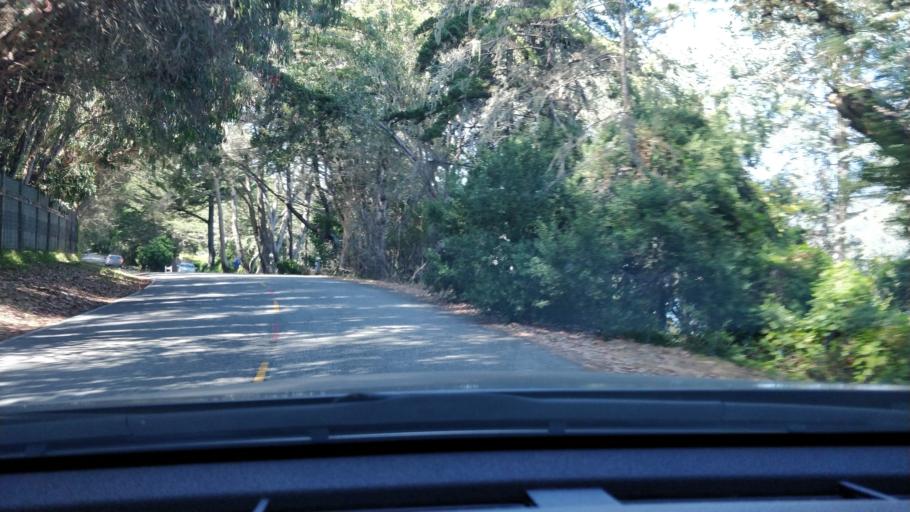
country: US
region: California
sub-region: Monterey County
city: Del Monte Forest
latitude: 36.5631
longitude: -121.9521
